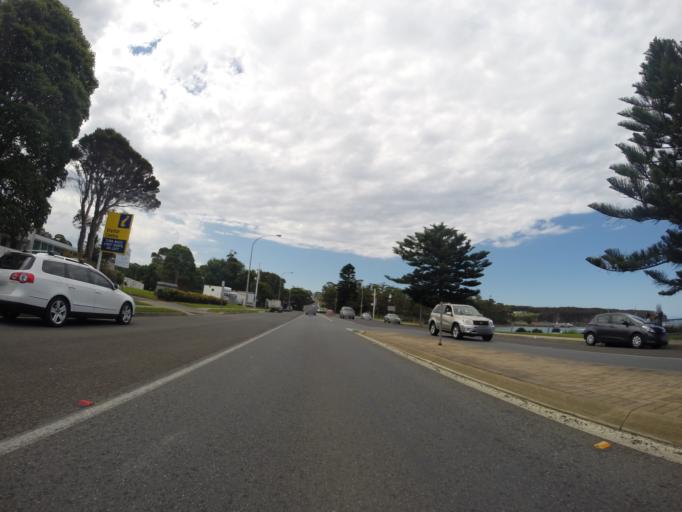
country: AU
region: New South Wales
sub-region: Shoalhaven Shire
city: Ulladulla
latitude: -35.3572
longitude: 150.4743
